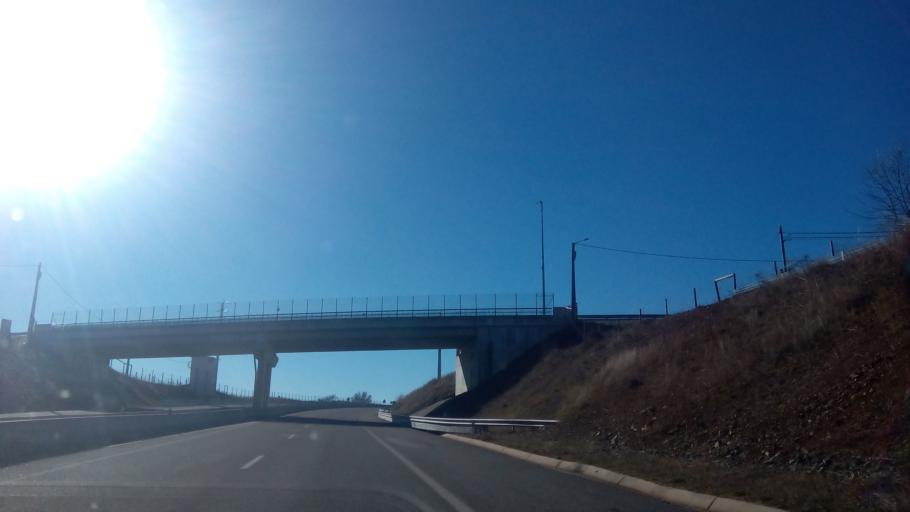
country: PT
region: Braganca
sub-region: Braganca Municipality
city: Braganca
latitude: 41.7711
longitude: -6.7593
